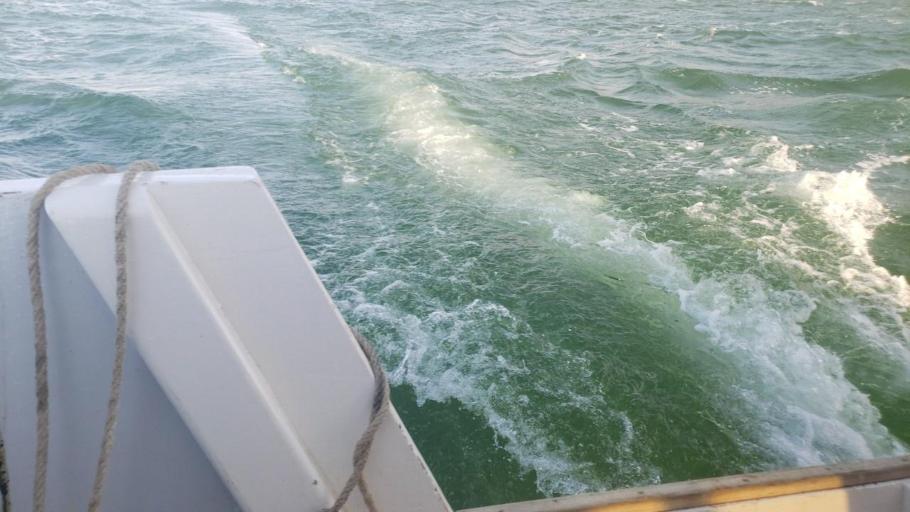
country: BO
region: La Paz
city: San Pablo
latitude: -16.2918
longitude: -68.7610
